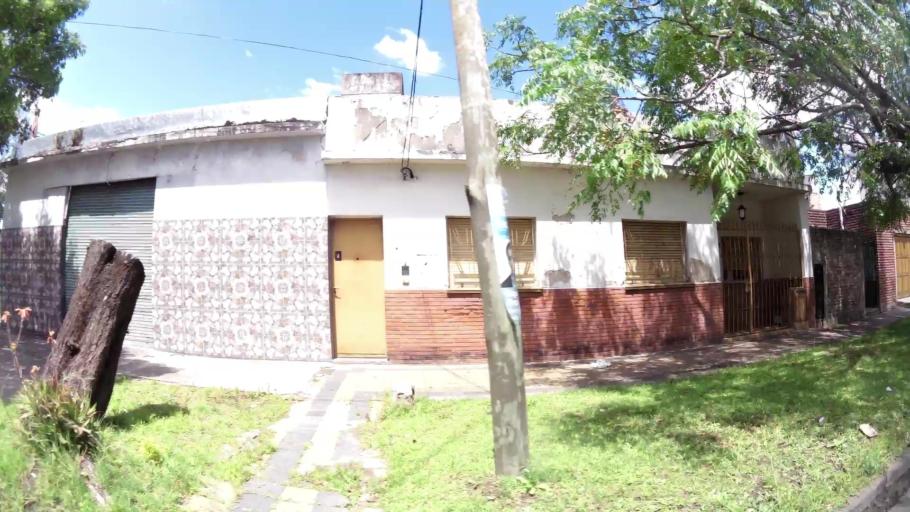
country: AR
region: Buenos Aires
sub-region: Partido de Lanus
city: Lanus
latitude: -34.7301
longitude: -58.4085
